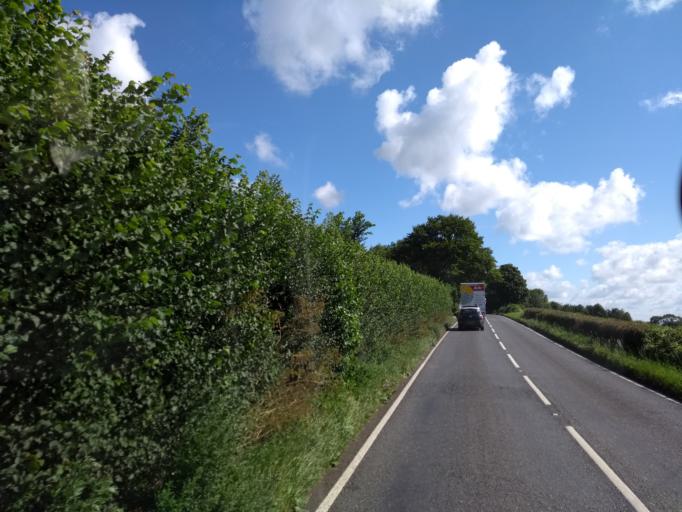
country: GB
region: England
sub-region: Somerset
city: Street
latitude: 51.1126
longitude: -2.7357
